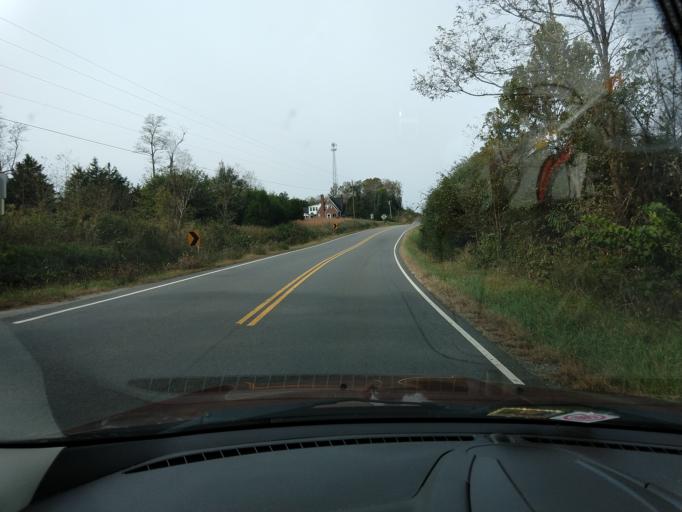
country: US
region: Virginia
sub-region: Franklin County
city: Union Hall
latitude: 36.9534
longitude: -79.5491
